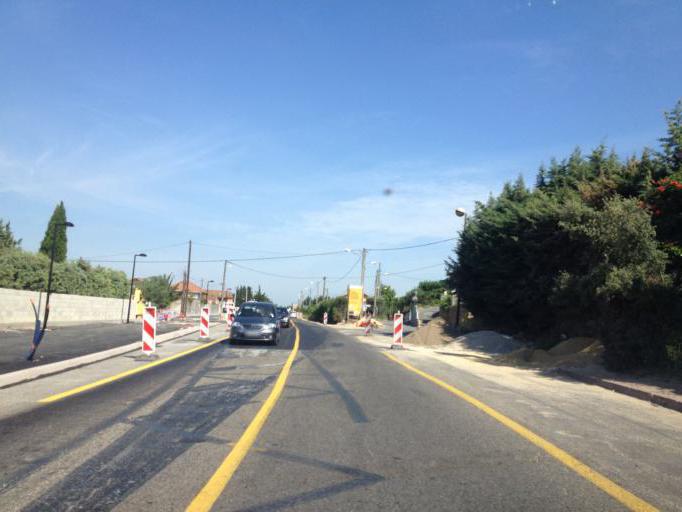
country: FR
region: Provence-Alpes-Cote d'Azur
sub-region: Departement du Vaucluse
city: Piolenc
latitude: 44.1802
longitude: 4.7589
